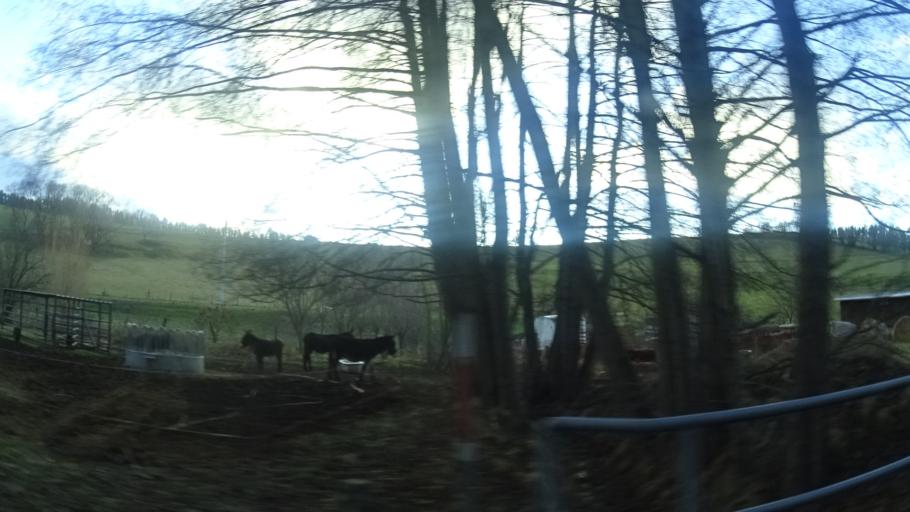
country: DE
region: Thuringia
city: Unterwellenborn
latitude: 50.6882
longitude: 11.4141
